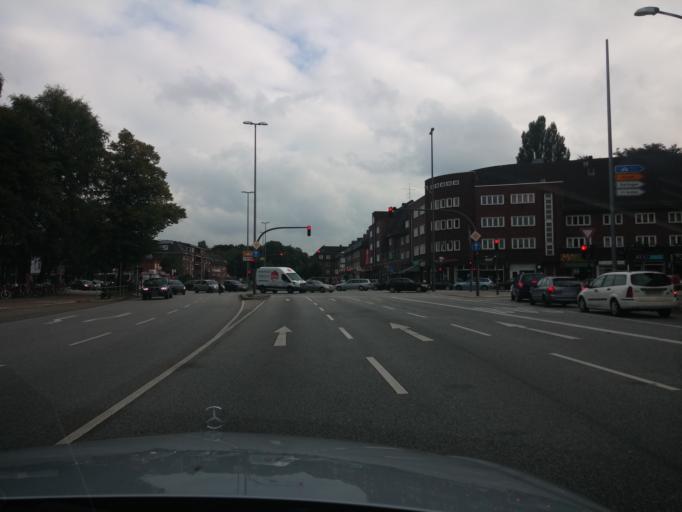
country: DE
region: Hamburg
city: Hamburg-Nord
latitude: 53.6004
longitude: 9.9634
